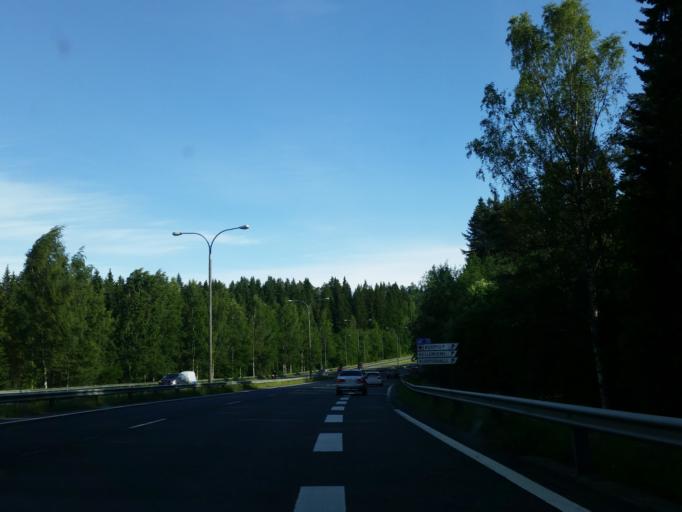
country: FI
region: Northern Savo
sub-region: Kuopio
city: Kuopio
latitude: 62.9113
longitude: 27.6860
